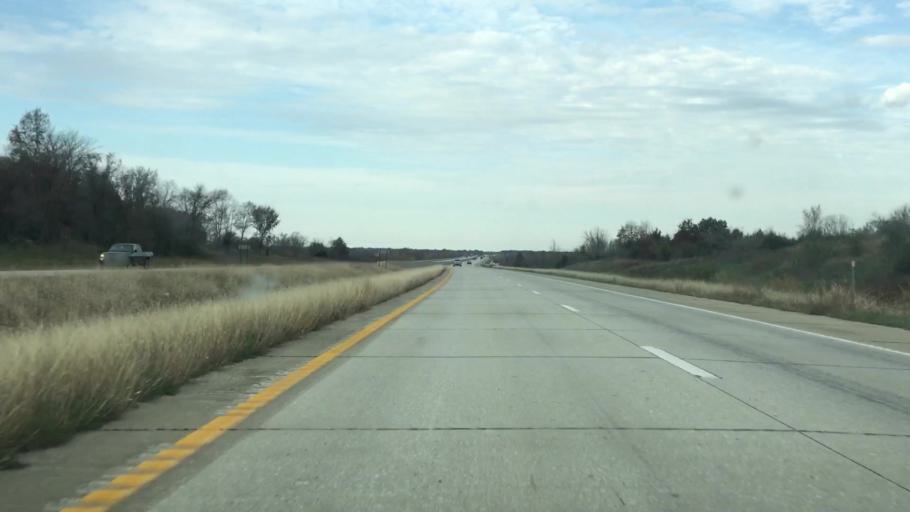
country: US
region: Missouri
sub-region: Henry County
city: Clinton
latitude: 38.3092
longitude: -93.7583
